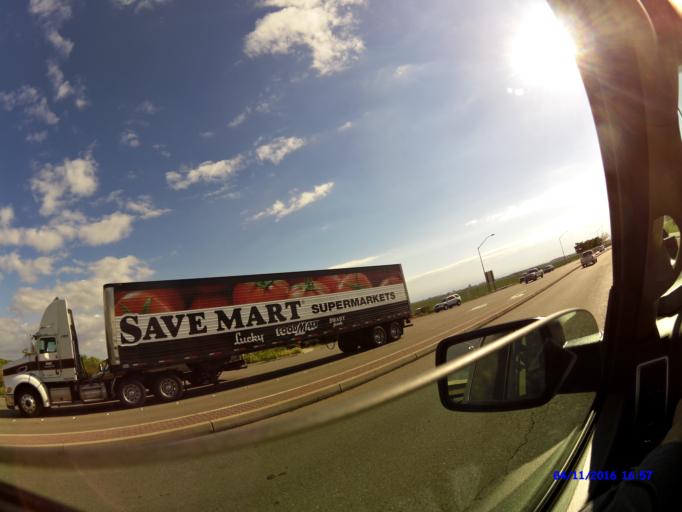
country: US
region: California
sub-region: San Joaquin County
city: Kennedy
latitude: 37.9046
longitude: -121.2240
